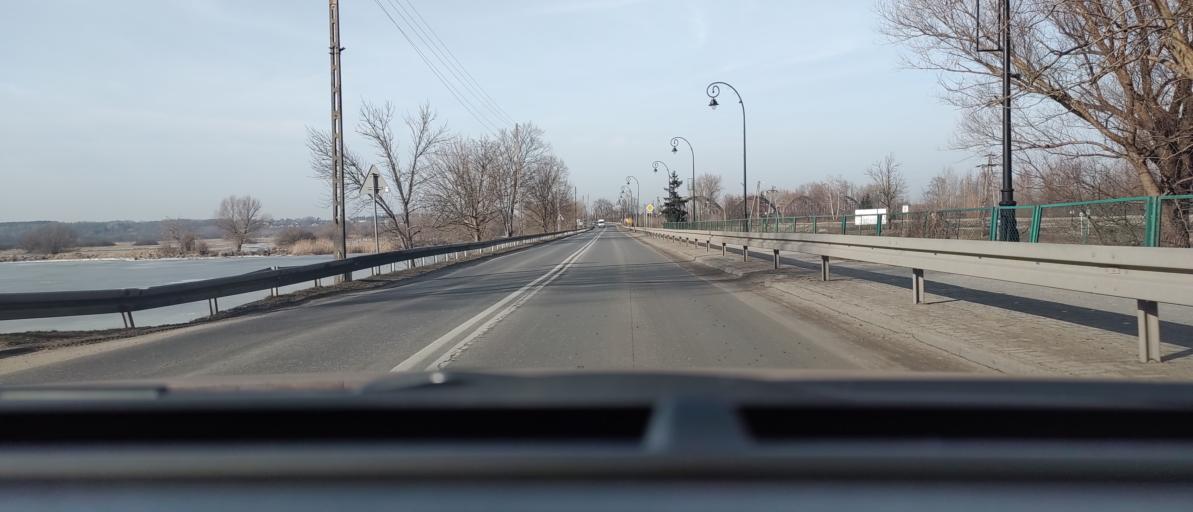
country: PL
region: Masovian Voivodeship
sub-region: Powiat bialobrzeski
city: Bialobrzegi
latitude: 51.6524
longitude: 20.9522
